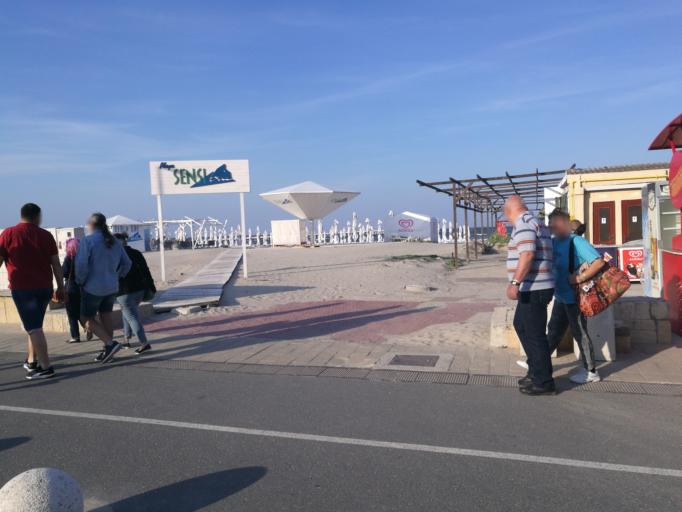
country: RO
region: Constanta
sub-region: Municipiul Constanta
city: Palazu Mare
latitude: 44.2292
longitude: 28.6285
